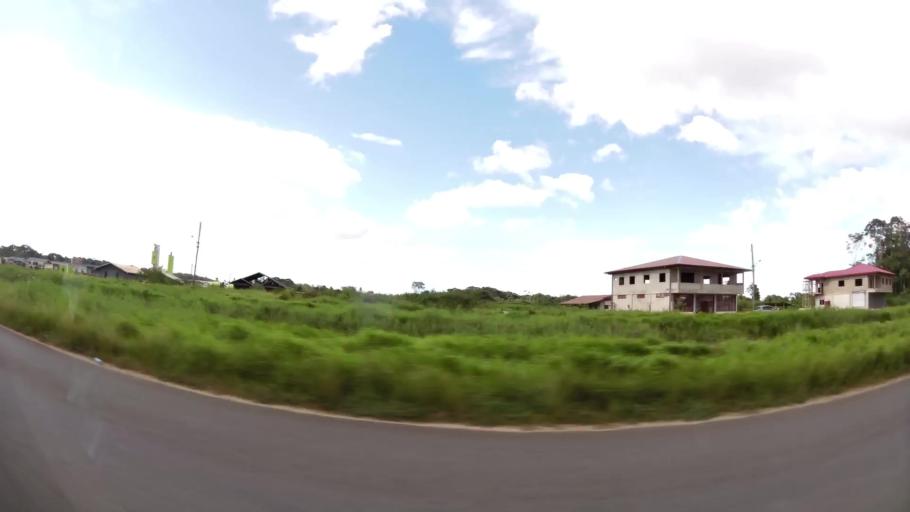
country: SR
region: Paramaribo
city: Paramaribo
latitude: 5.8572
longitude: -55.1736
